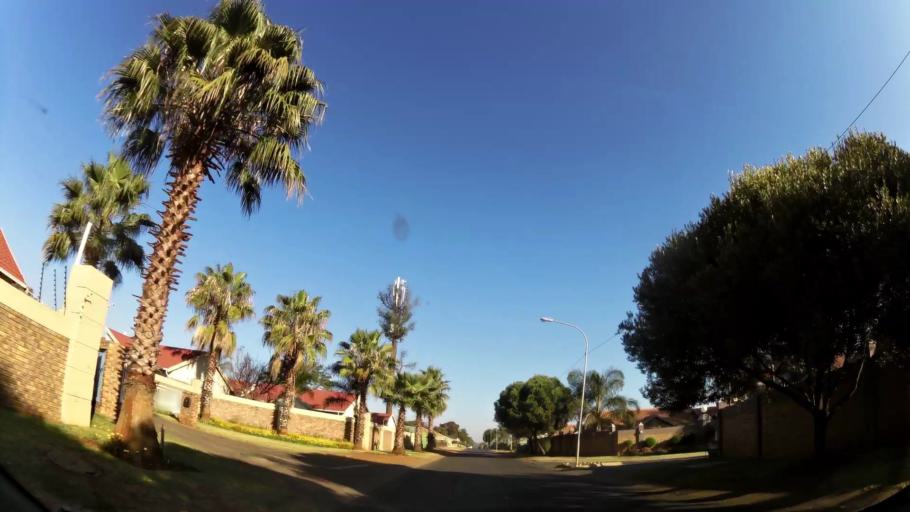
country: ZA
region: Gauteng
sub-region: City of Tshwane Metropolitan Municipality
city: Centurion
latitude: -25.8498
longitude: 28.1543
